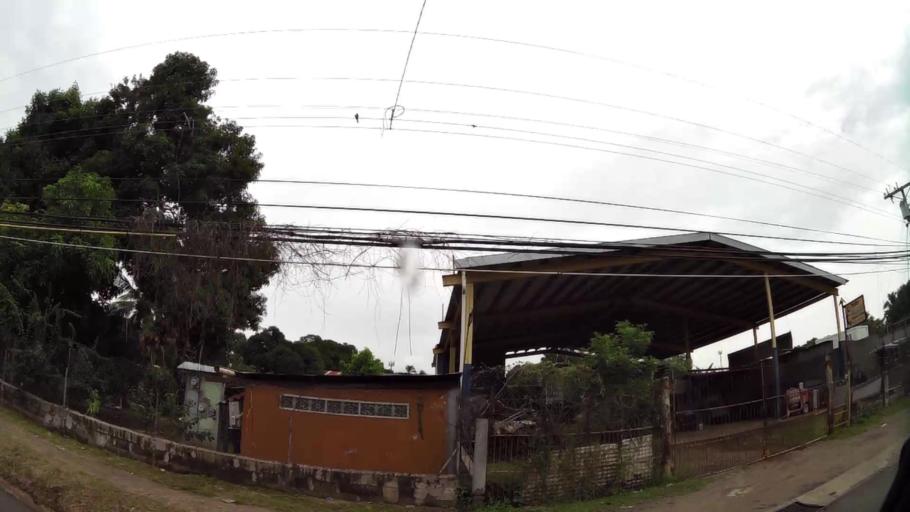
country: PA
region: Panama
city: San Miguelito
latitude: 9.0457
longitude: -79.4384
